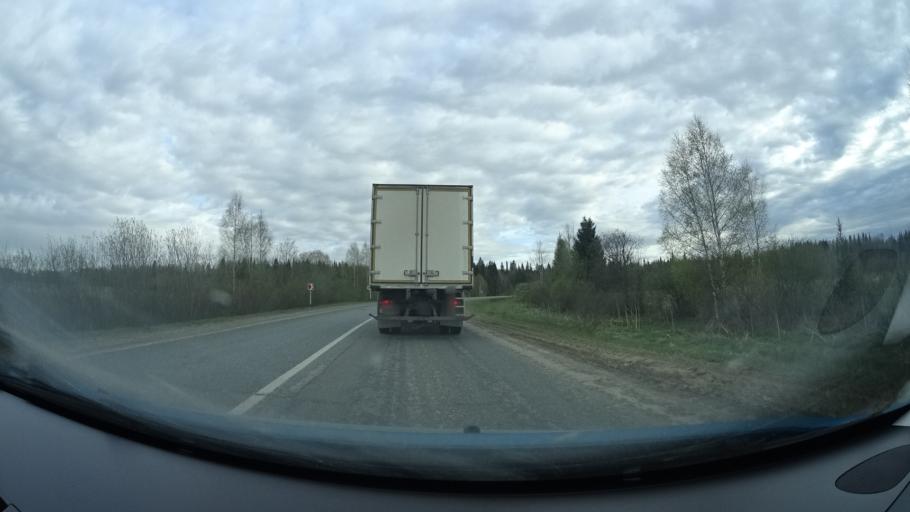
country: RU
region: Perm
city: Yugo-Kamskiy
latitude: 57.5346
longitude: 55.6896
